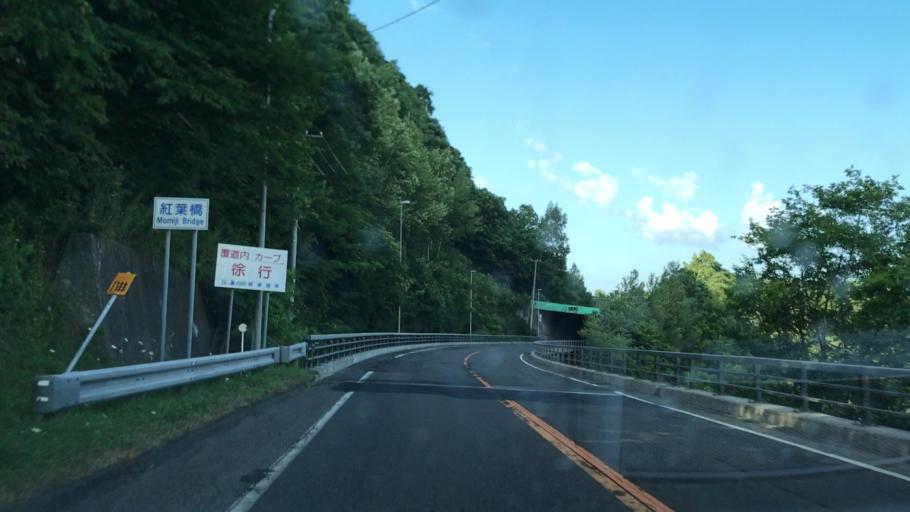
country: JP
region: Hokkaido
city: Shizunai-furukawacho
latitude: 42.8407
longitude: 142.4161
